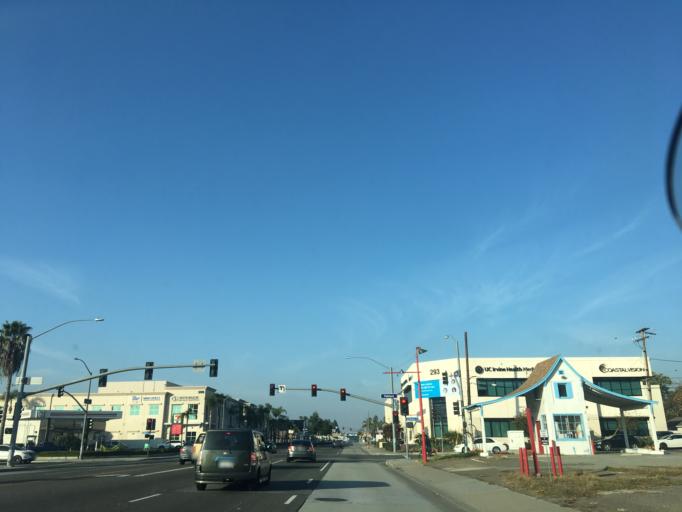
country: US
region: California
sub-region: Orange County
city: Orange
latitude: 33.7834
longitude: -117.8672
